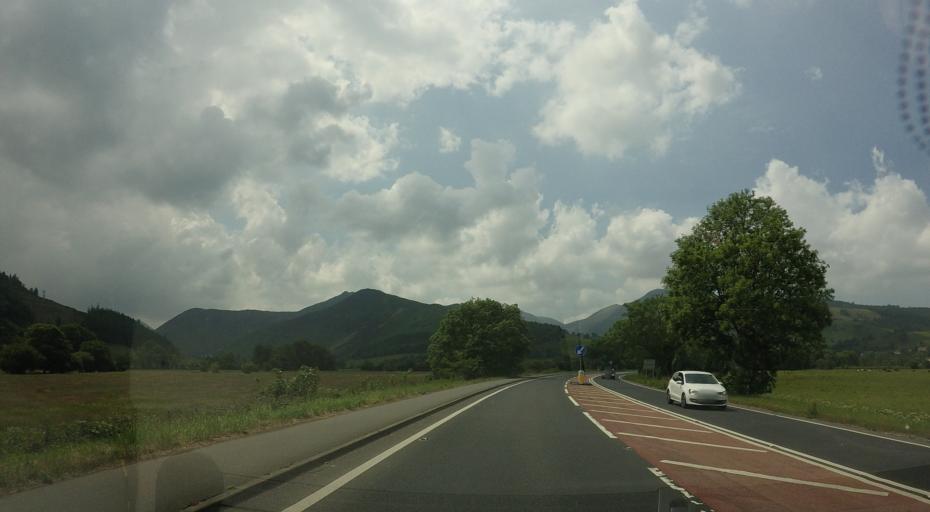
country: GB
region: England
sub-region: Cumbria
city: Keswick
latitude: 54.6012
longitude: -3.1705
